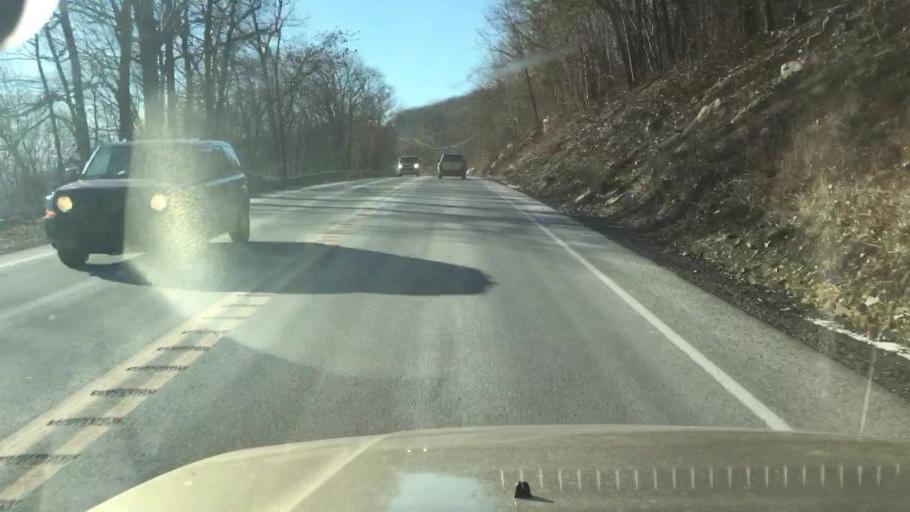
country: US
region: Pennsylvania
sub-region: Luzerne County
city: Conyngham
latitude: 41.0311
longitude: -76.0905
